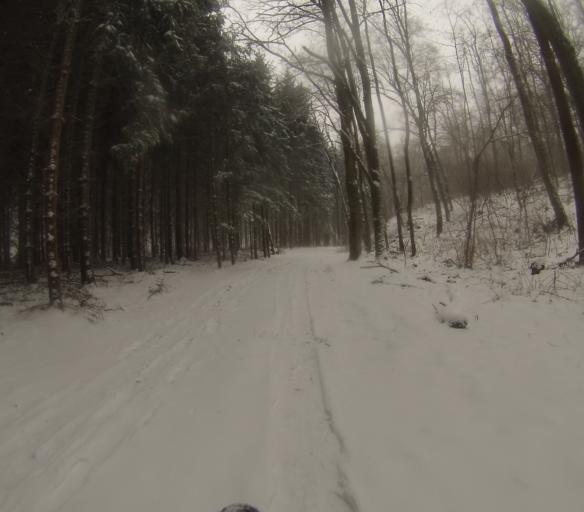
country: CZ
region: South Moravian
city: Strelice
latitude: 49.1312
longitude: 16.5097
